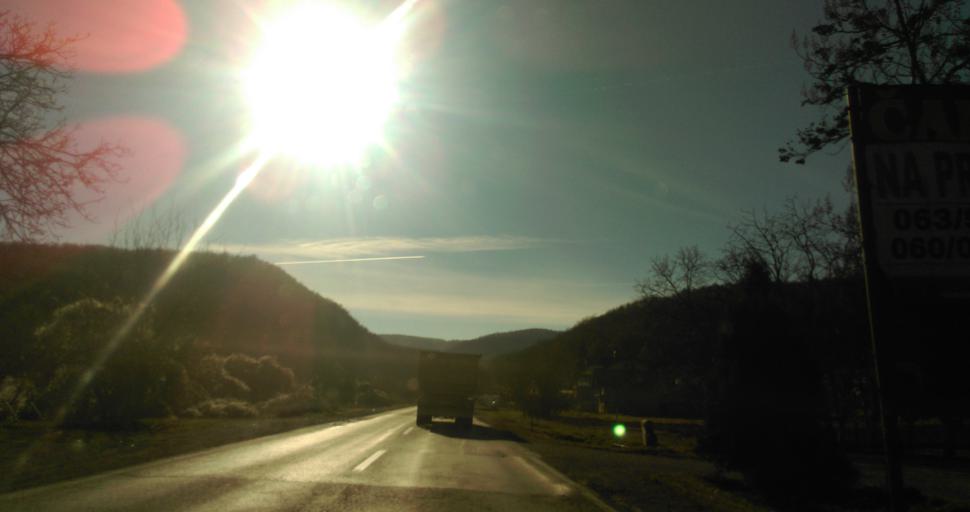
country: RS
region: Autonomna Pokrajina Vojvodina
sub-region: Juznobacki Okrug
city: Novi Sad
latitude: 45.1900
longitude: 19.8405
